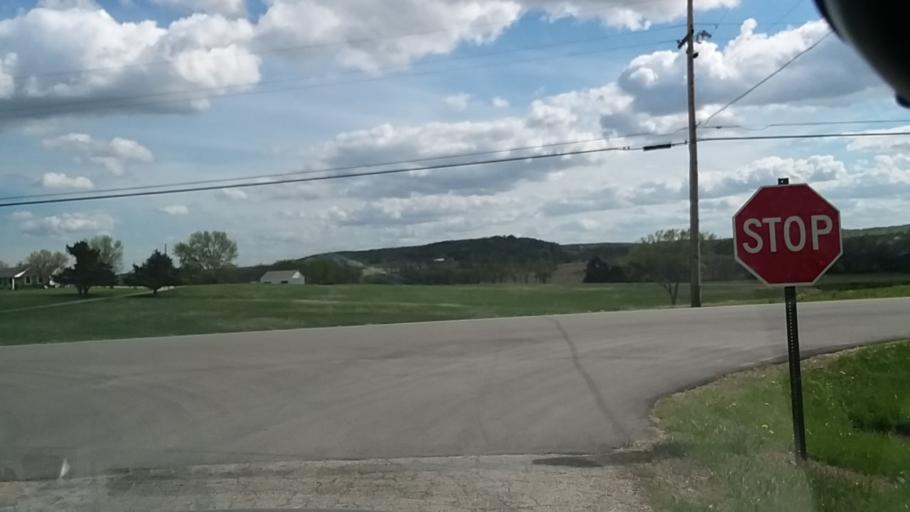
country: US
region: Kansas
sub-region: Douglas County
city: Lawrence
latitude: 38.8993
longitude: -95.2478
